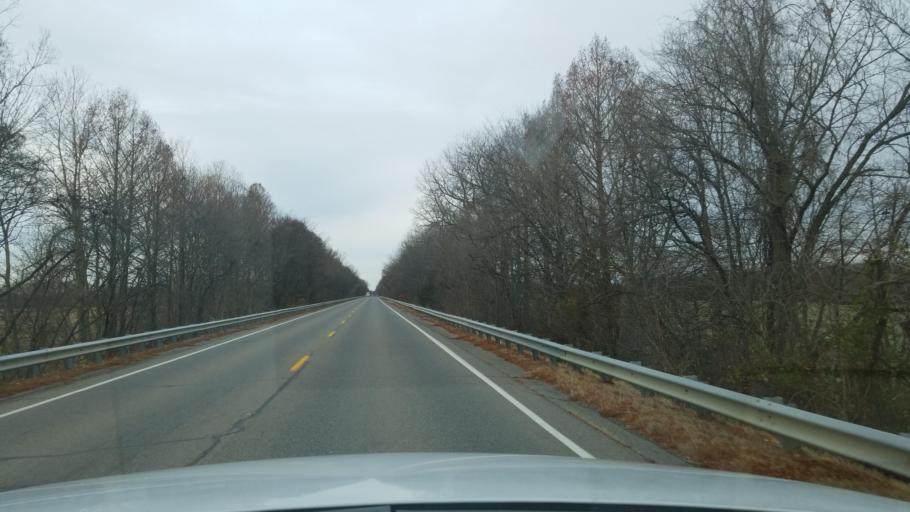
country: US
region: Indiana
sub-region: Posey County
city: Mount Vernon
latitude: 37.9291
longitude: -87.9685
